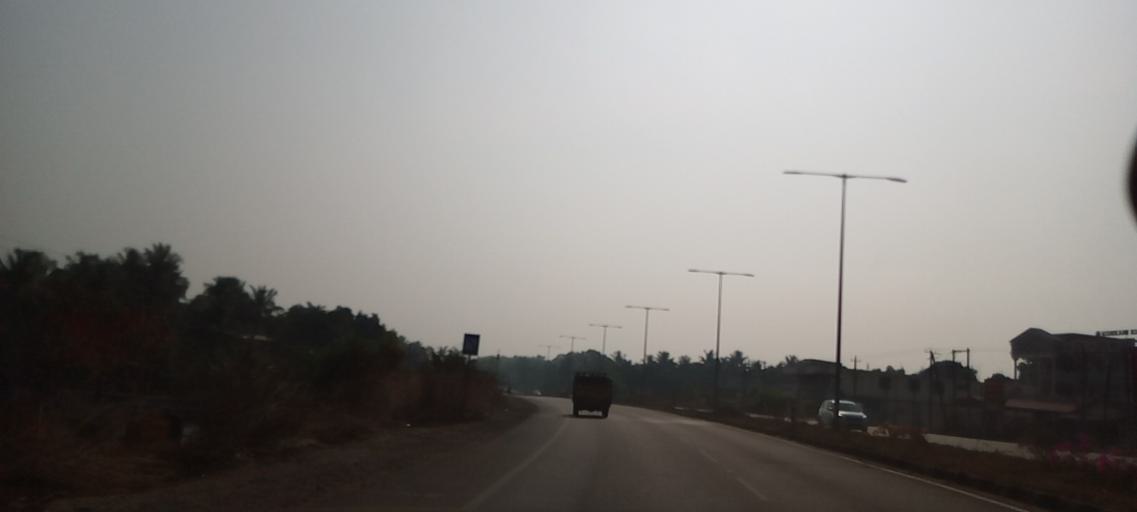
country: IN
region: Karnataka
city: Gangolli
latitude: 13.6882
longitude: 74.6554
